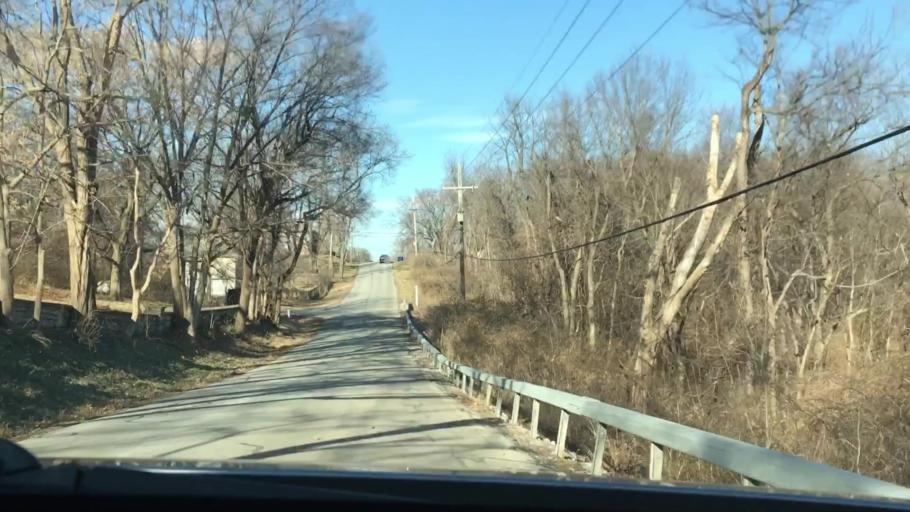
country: US
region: Missouri
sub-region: Platte County
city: Parkville
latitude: 39.2014
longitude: -94.6872
